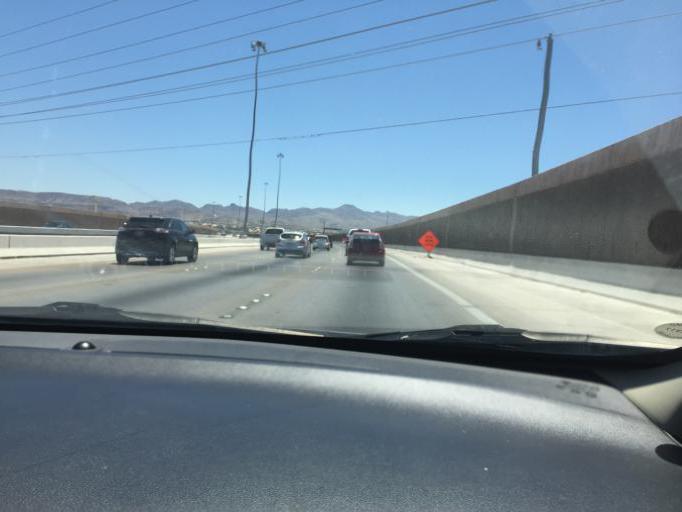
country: US
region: Nevada
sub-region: Clark County
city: Whitney
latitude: 36.0283
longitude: -115.1306
